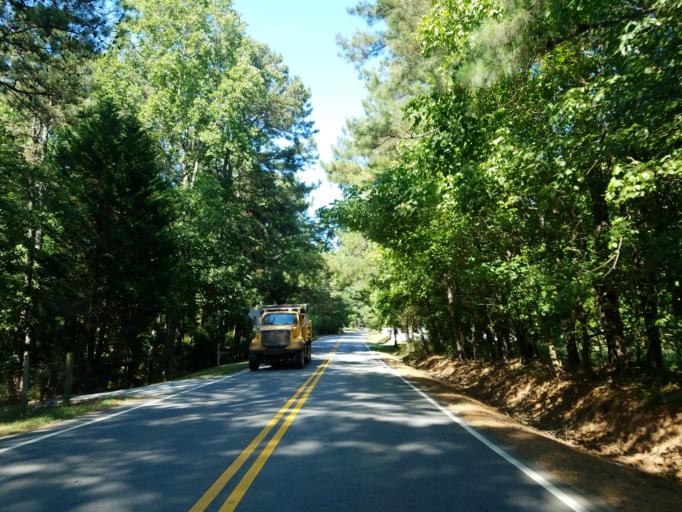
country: US
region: Georgia
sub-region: Fulton County
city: Milton
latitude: 34.1558
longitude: -84.3371
